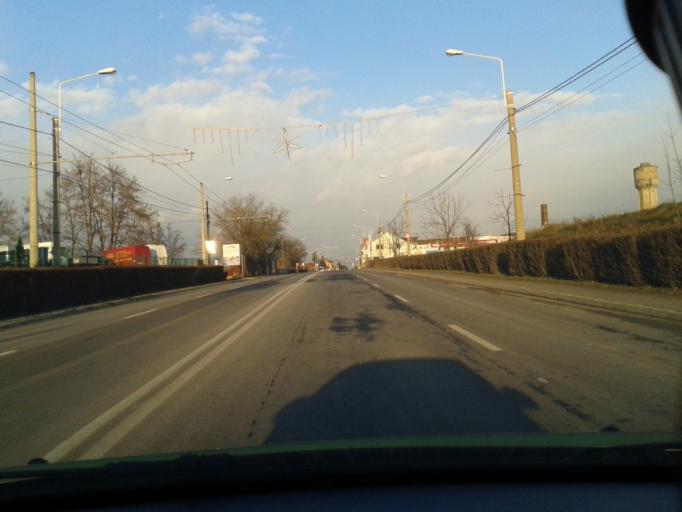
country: RO
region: Sibiu
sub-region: Municipiul Medias
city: Medias
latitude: 46.1468
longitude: 24.3246
